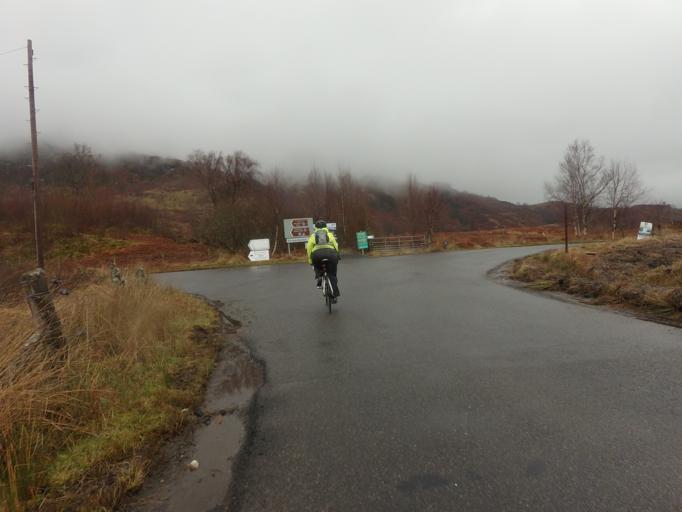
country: GB
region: Scotland
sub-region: West Dunbartonshire
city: Balloch
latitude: 56.2538
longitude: -4.5898
